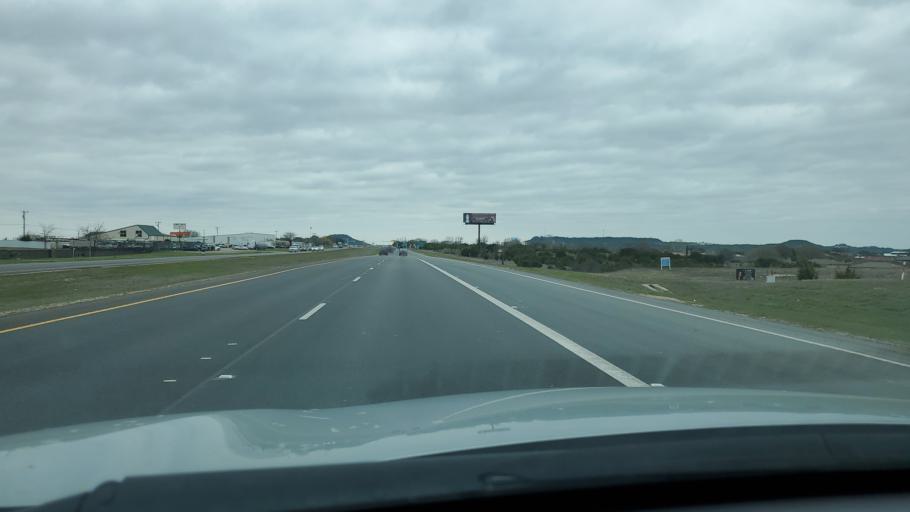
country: US
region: Texas
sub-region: Bell County
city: Killeen
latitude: 31.0164
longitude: -97.7529
